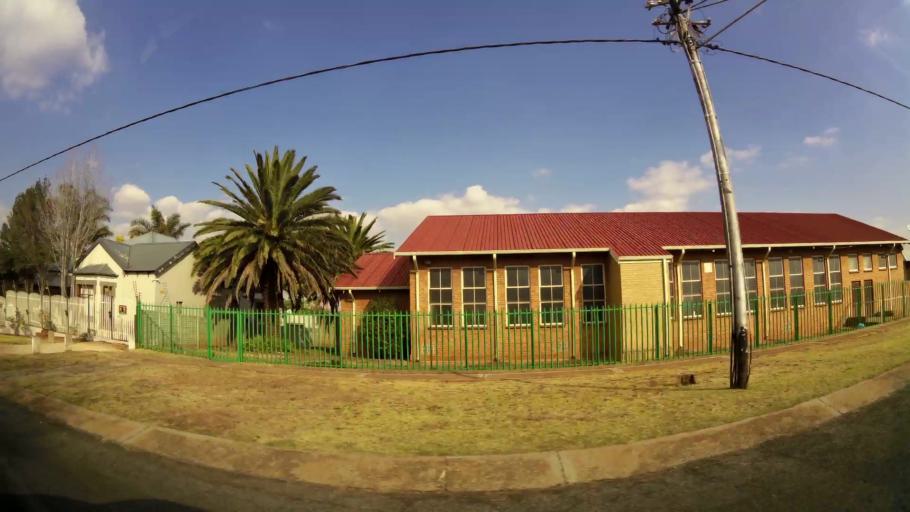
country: ZA
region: Gauteng
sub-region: West Rand District Municipality
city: Krugersdorp
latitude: -26.0890
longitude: 27.7727
